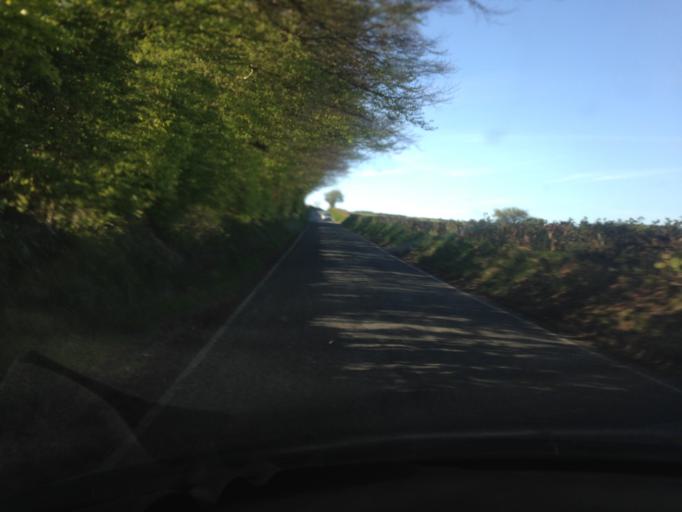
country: GB
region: Wales
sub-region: County of Ceredigion
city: Newcastle Emlyn
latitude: 52.1238
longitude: -4.4427
